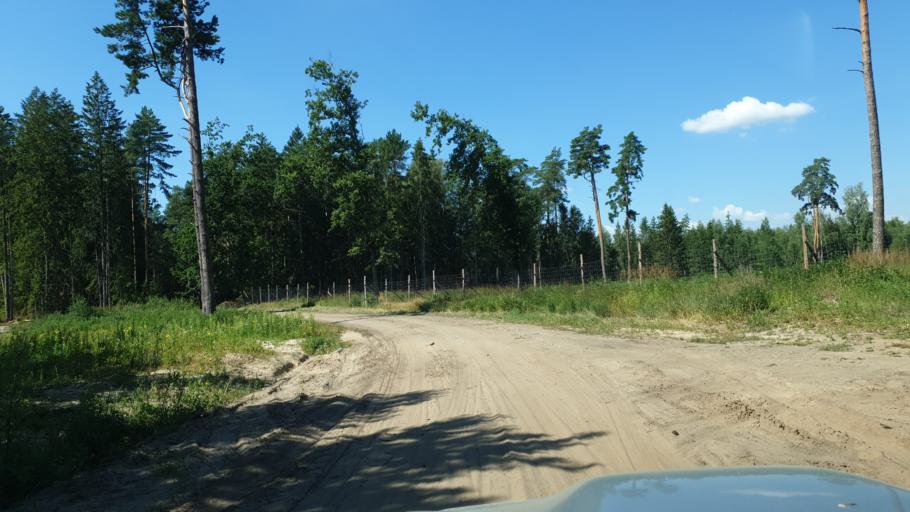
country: LT
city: Sirvintos
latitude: 54.9100
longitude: 24.9362
